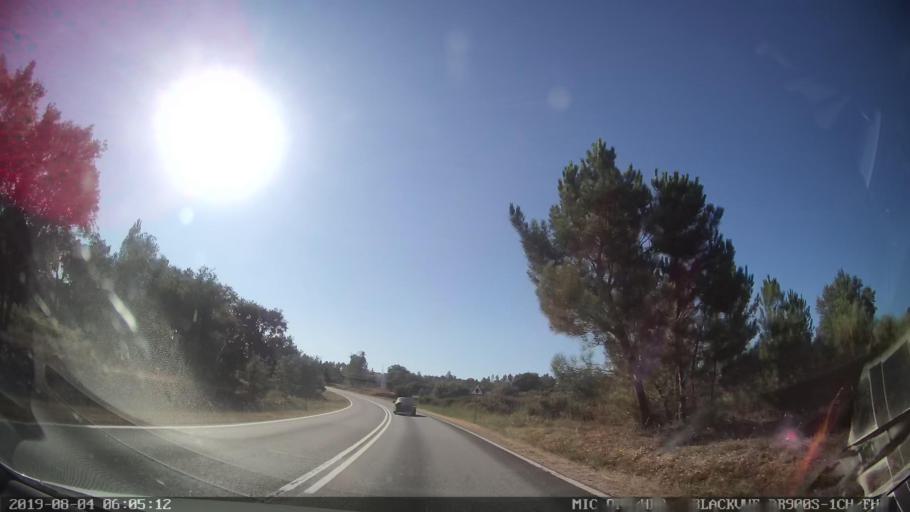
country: PT
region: Santarem
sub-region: Abrantes
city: Alferrarede
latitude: 39.4749
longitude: -8.0732
